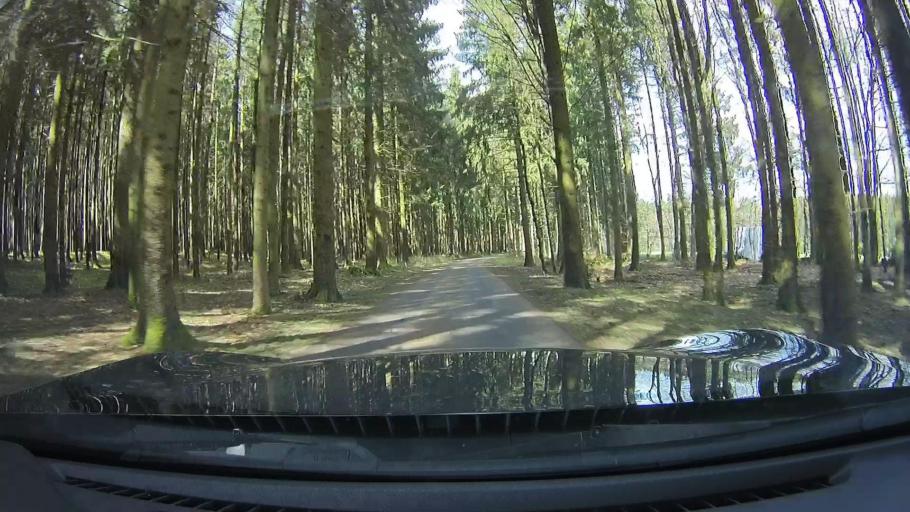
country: DE
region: Hesse
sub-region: Regierungsbezirk Darmstadt
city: Hesseneck
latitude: 49.5882
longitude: 9.0889
